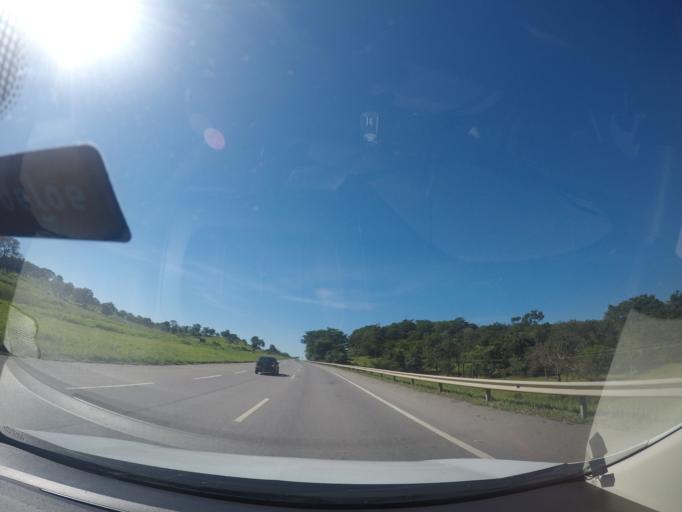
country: BR
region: Goias
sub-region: Morrinhos
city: Morrinhos
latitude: -17.5826
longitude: -49.1960
